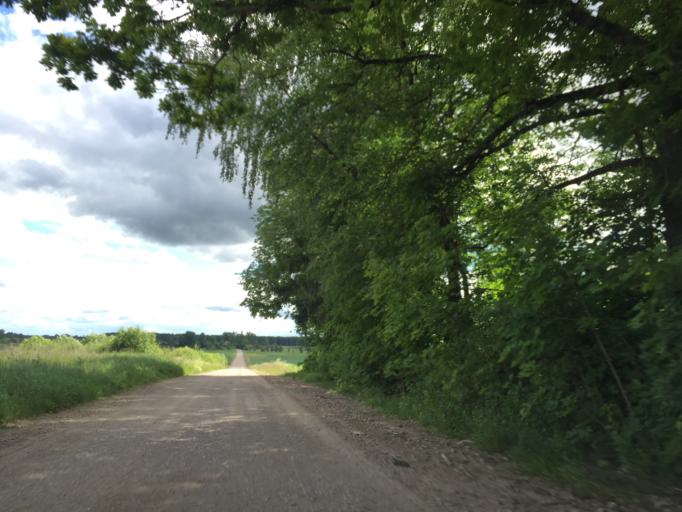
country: LV
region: Vecumnieki
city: Vecumnieki
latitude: 56.4795
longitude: 24.4163
